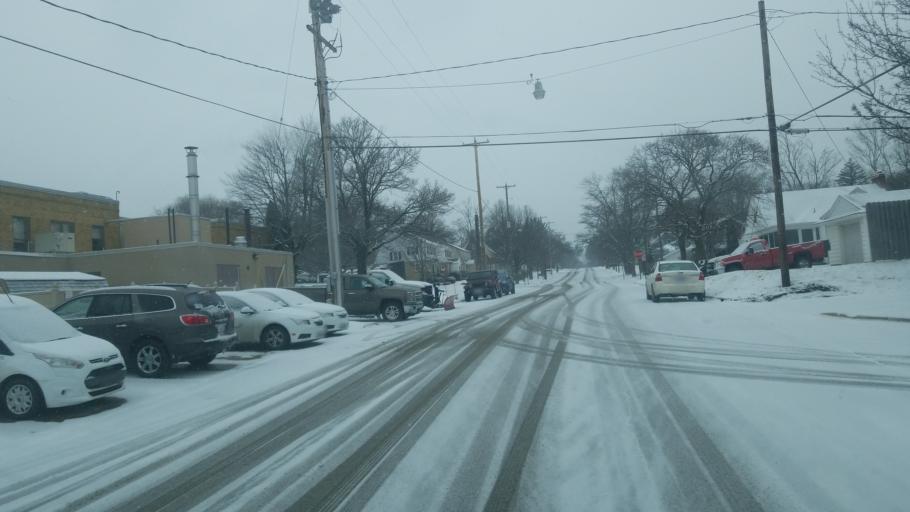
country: US
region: Michigan
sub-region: Mecosta County
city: Big Rapids
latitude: 43.6944
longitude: -85.4748
